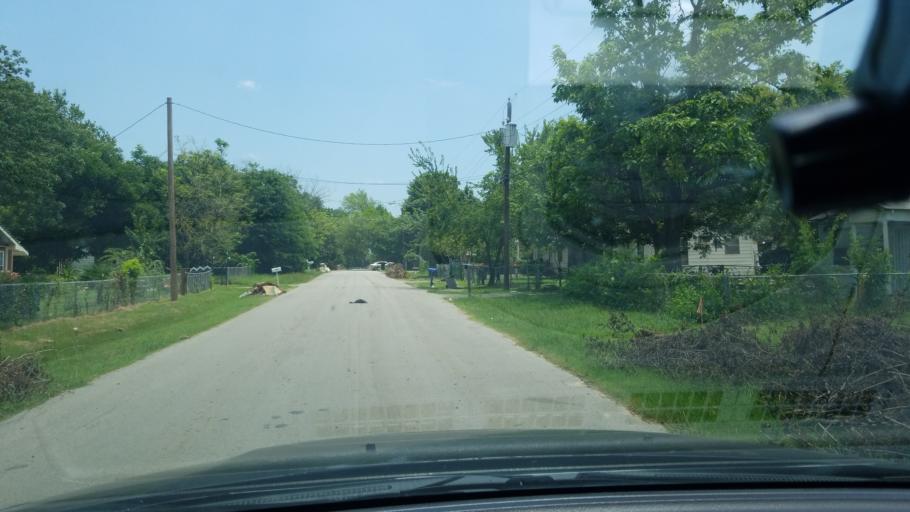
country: US
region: Texas
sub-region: Dallas County
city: Balch Springs
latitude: 32.7170
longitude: -96.6524
